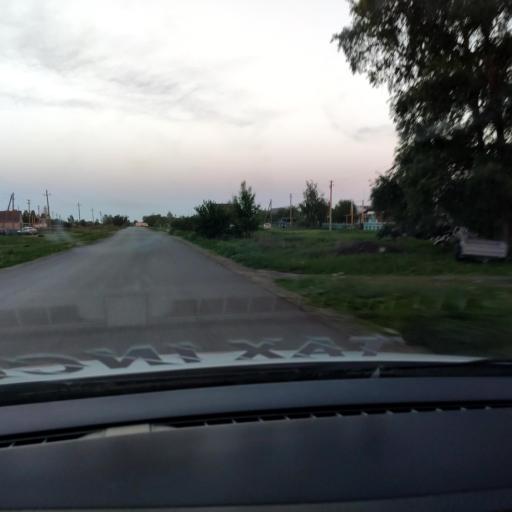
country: RU
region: Voronezj
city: Novovoronezh
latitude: 51.4117
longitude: 39.3082
